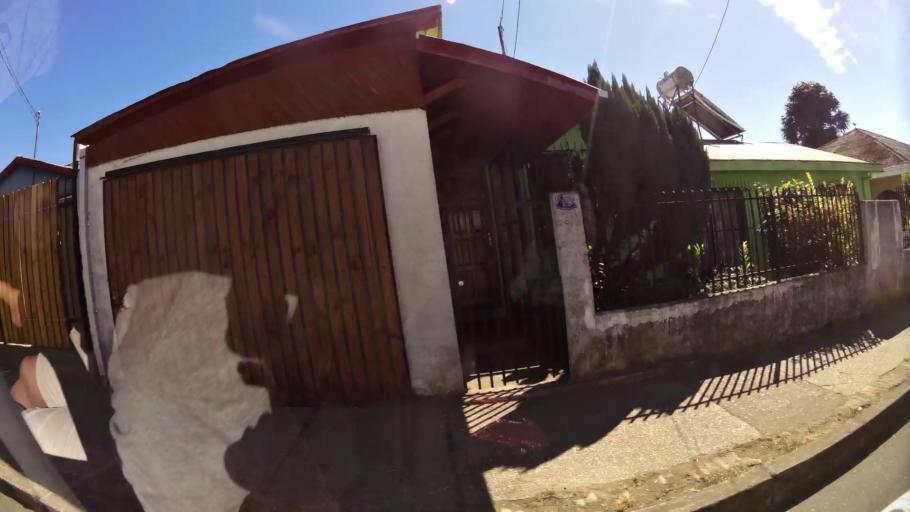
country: CL
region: Biobio
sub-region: Provincia de Concepcion
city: Penco
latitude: -36.7414
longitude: -72.9965
